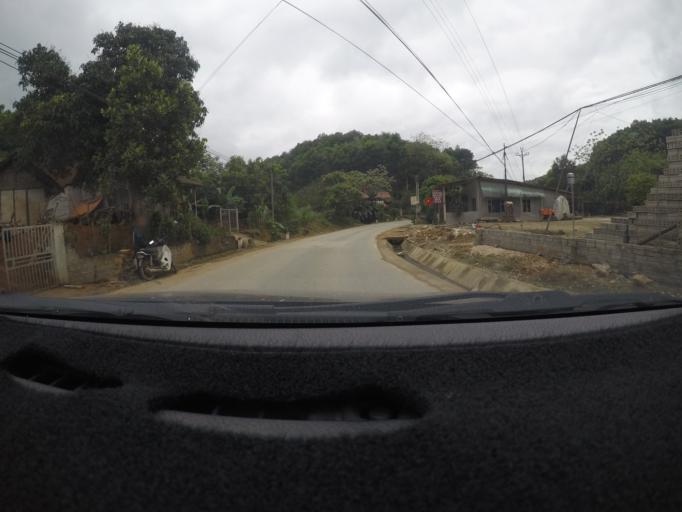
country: VN
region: Yen Bai
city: Co Phuc
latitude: 21.9165
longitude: 104.8077
